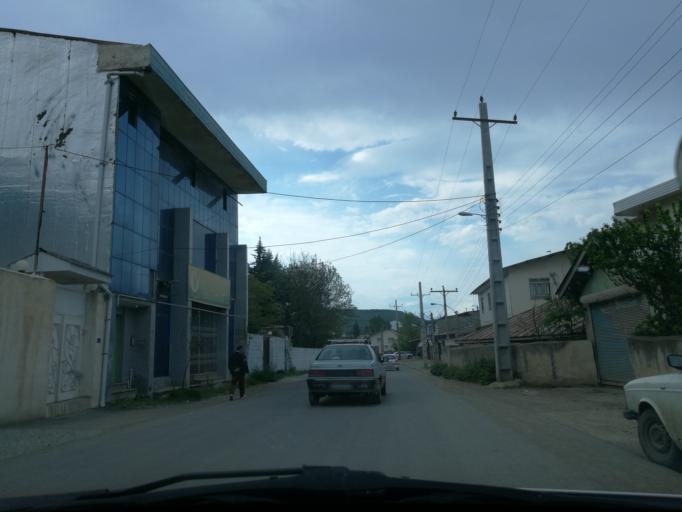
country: IR
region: Mazandaran
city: Chalus
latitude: 36.5296
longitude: 51.2295
